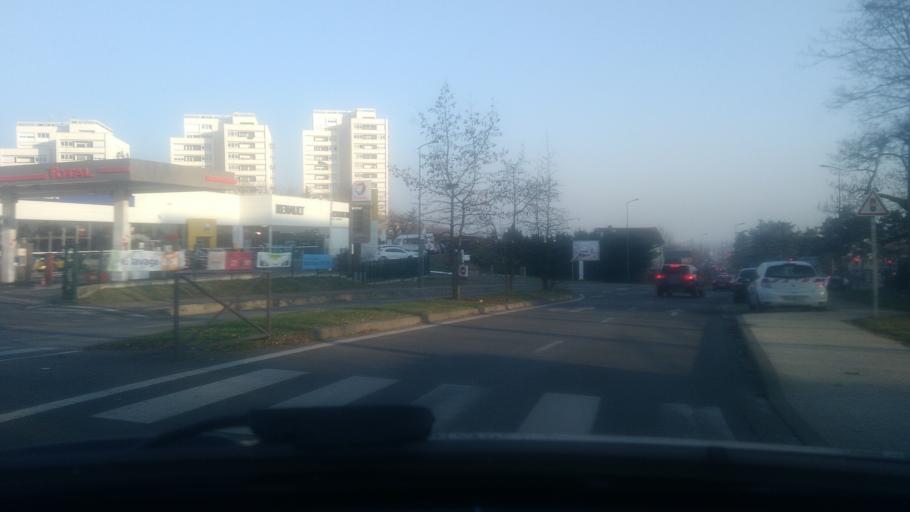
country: FR
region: Ile-de-France
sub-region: Departement du Val-d'Oise
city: Cergy-Pontoise
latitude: 49.0496
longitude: 2.0747
